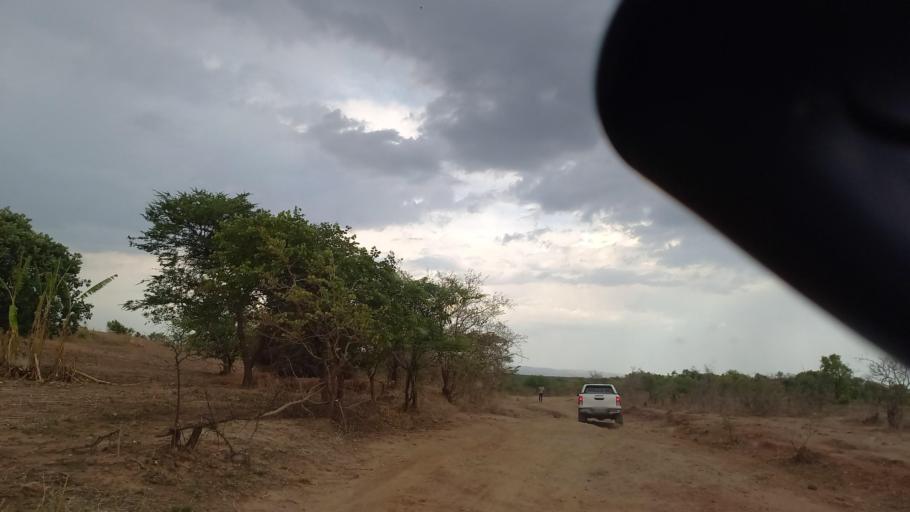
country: ZM
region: Lusaka
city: Kafue
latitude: -16.1222
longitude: 28.0620
